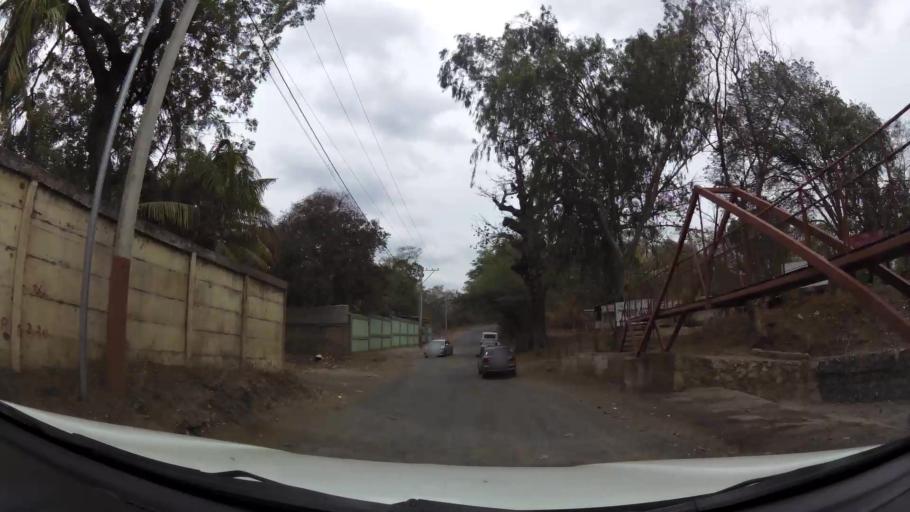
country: NI
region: Masaya
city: Ticuantepe
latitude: 12.0760
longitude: -86.1786
